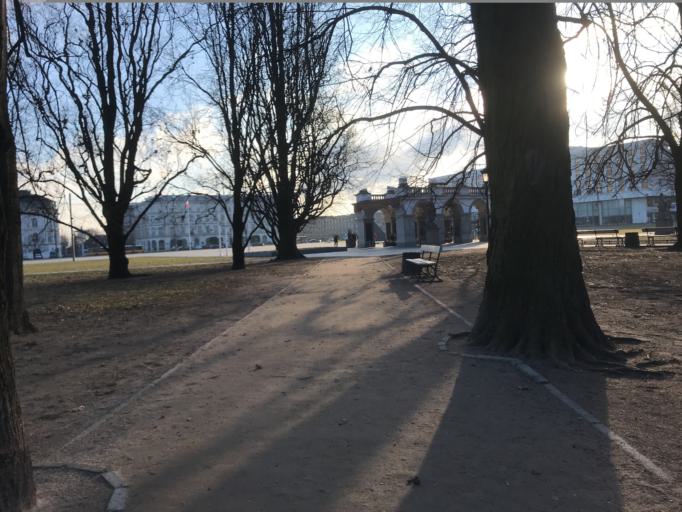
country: PL
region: Masovian Voivodeship
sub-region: Warszawa
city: Warsaw
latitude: 52.2413
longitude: 21.0103
